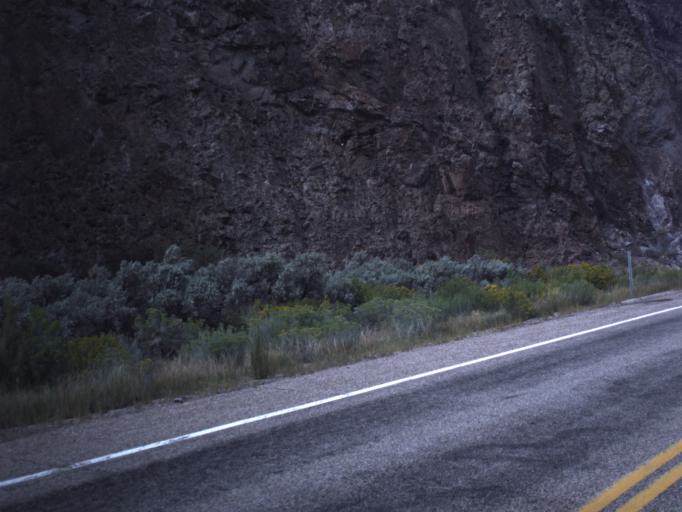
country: US
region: Utah
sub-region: Piute County
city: Junction
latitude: 38.1056
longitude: -112.3364
